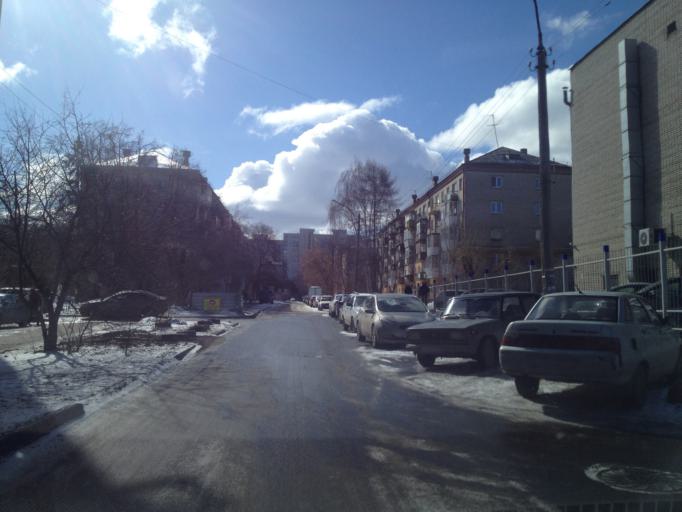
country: RU
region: Sverdlovsk
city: Yekaterinburg
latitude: 56.8121
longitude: 60.6034
